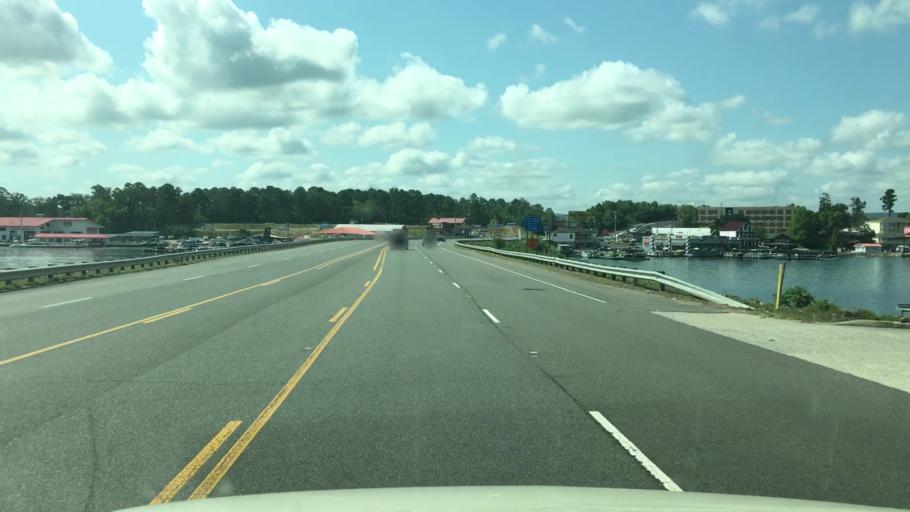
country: US
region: Arkansas
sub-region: Garland County
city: Lake Hamilton
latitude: 34.4426
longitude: -93.0893
